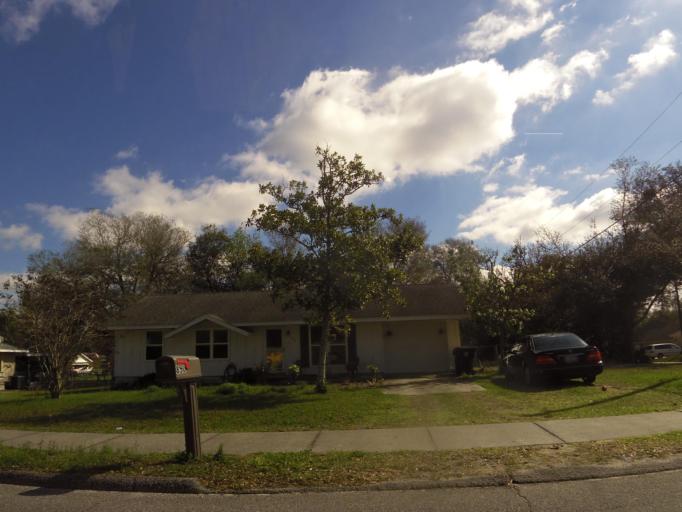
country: US
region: Florida
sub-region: Volusia County
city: Orange City
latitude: 28.9396
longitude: -81.3071
